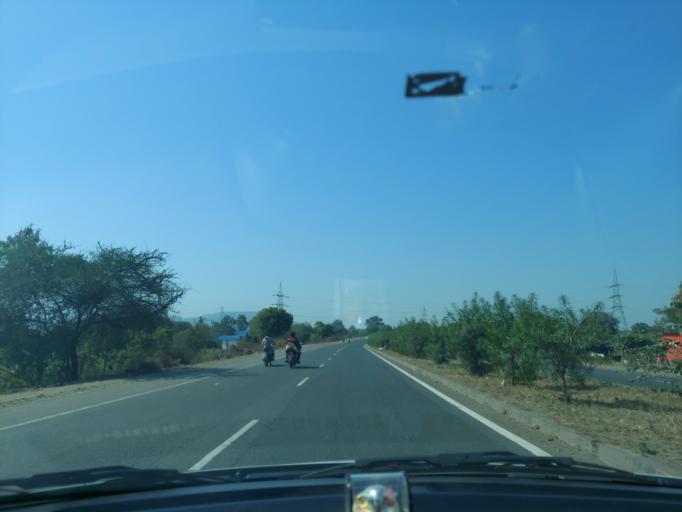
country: IN
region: Madhya Pradesh
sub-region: Indore
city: Manpur
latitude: 22.4250
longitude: 75.6091
